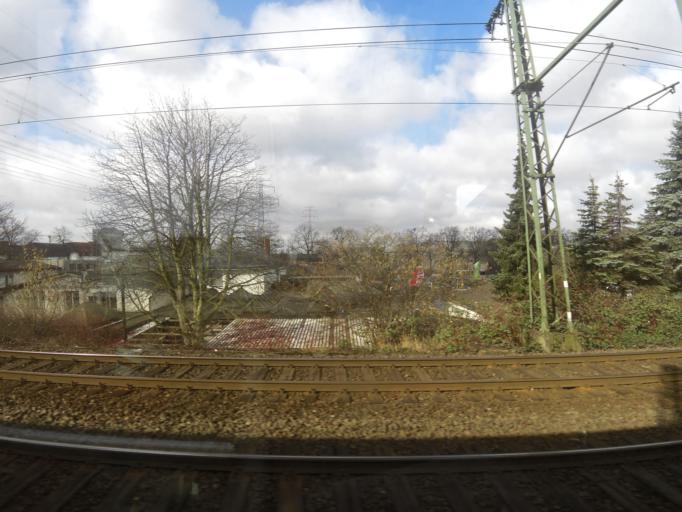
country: DE
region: Hamburg
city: Harburg
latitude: 53.4672
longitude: 9.9955
